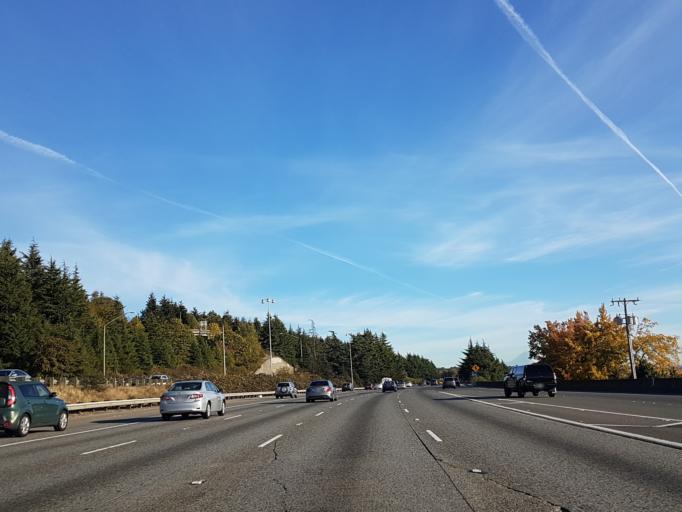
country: US
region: Washington
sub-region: King County
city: White Center
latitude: 47.5469
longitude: -122.3097
